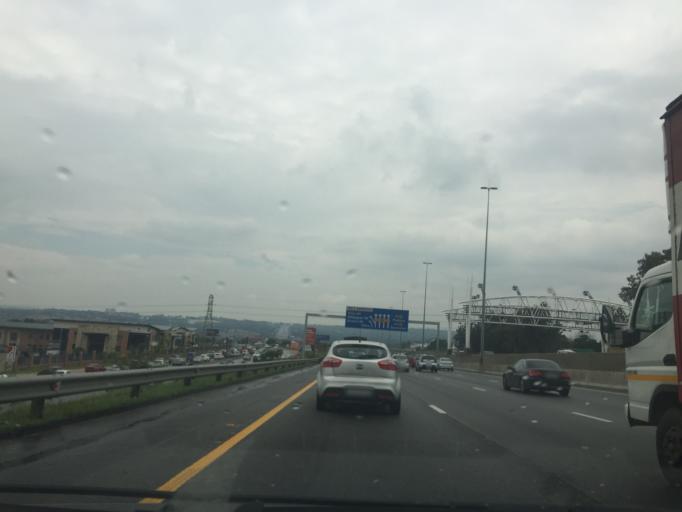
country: ZA
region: Gauteng
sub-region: City of Johannesburg Metropolitan Municipality
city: Midrand
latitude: -26.0359
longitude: 28.0433
